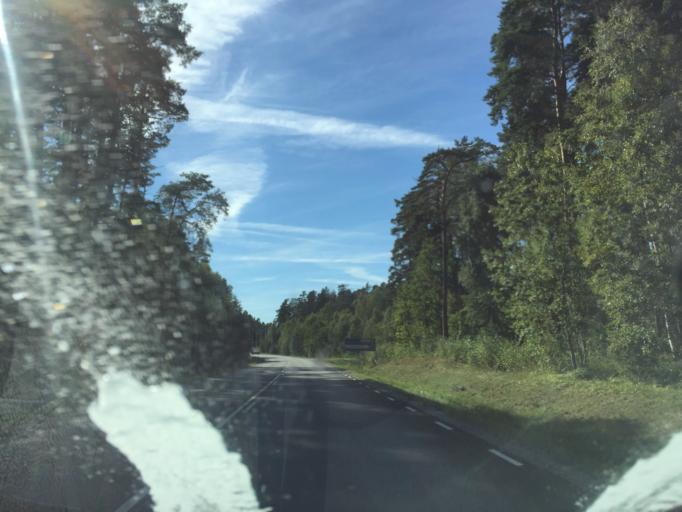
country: SE
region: OErebro
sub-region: Orebro Kommun
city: Orebro
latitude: 59.3003
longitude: 15.2562
